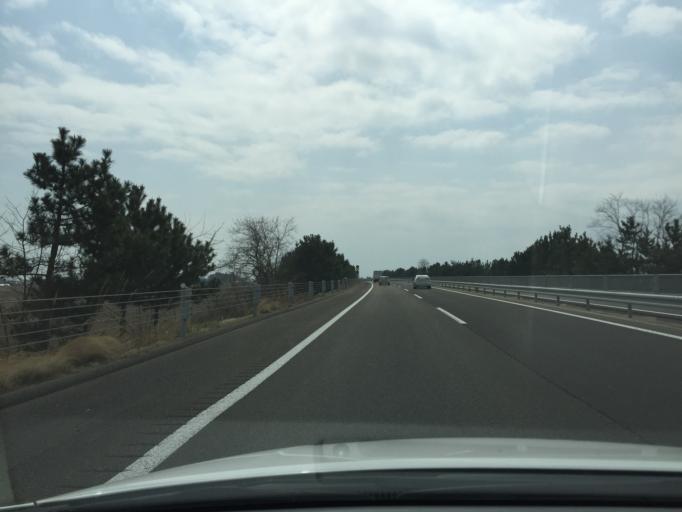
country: JP
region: Miyagi
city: Iwanuma
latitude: 38.1236
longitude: 140.8868
